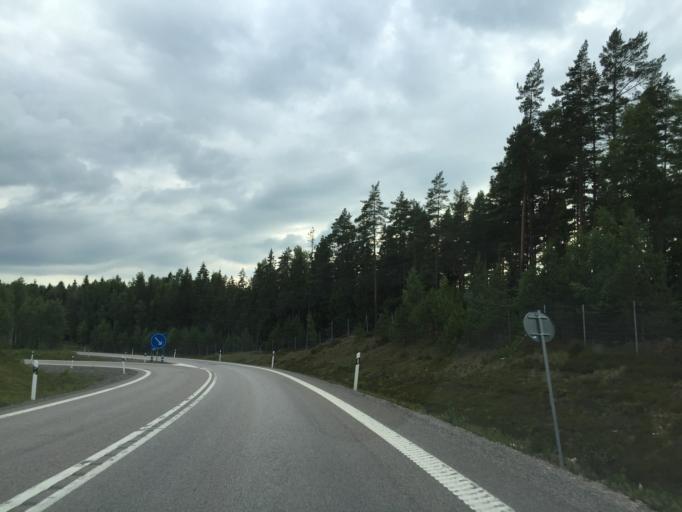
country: SE
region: OErebro
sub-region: Lindesbergs Kommun
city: Fellingsbro
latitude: 59.3403
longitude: 15.5389
